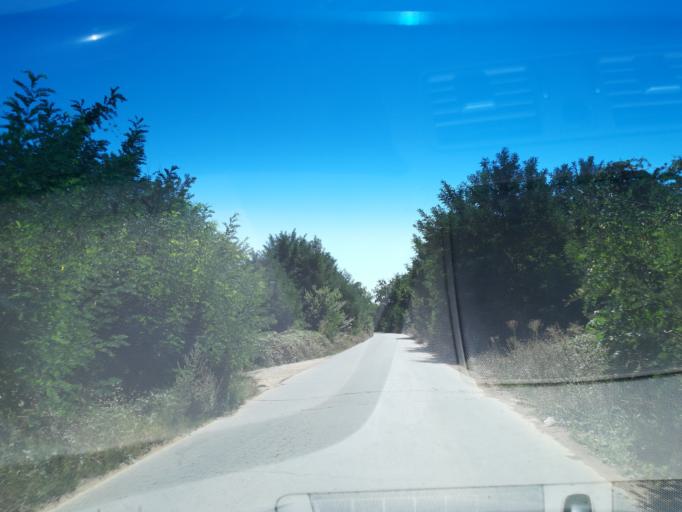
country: BG
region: Pazardzhik
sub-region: Obshtina Pazardzhik
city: Pazardzhik
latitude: 42.2907
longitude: 24.3952
